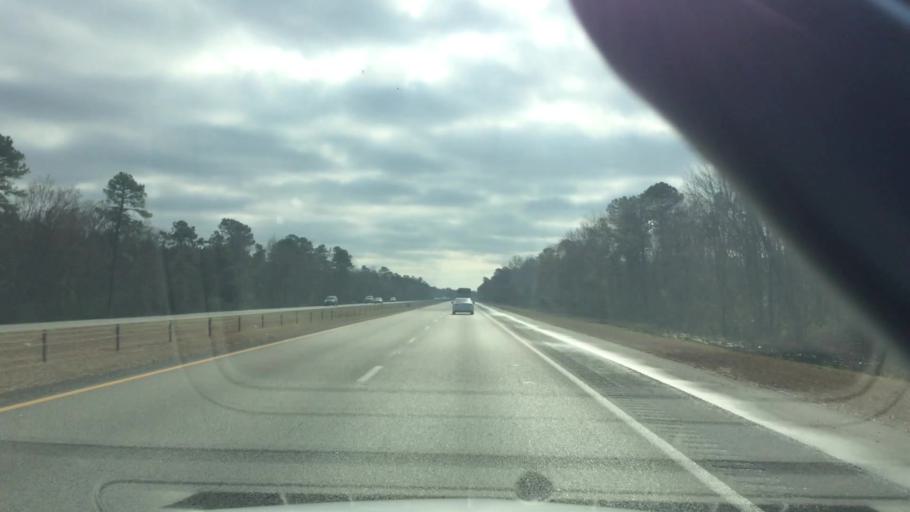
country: US
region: North Carolina
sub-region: Pender County
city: Rocky Point
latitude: 34.4052
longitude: -77.8719
